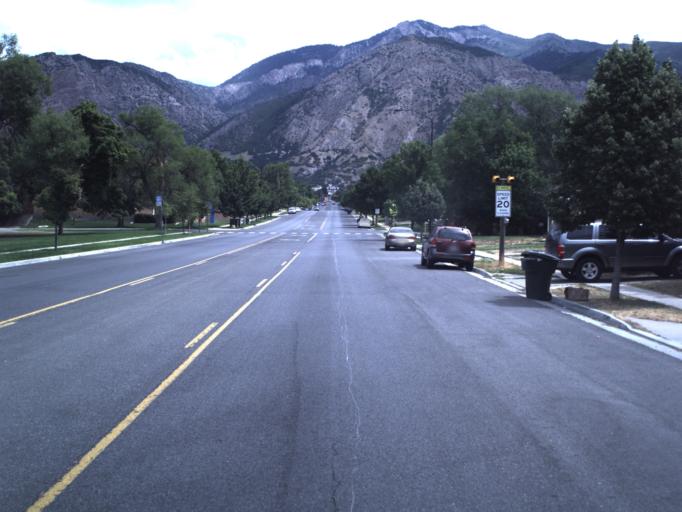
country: US
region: Utah
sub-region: Weber County
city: Ogden
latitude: 41.2100
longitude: -111.9581
